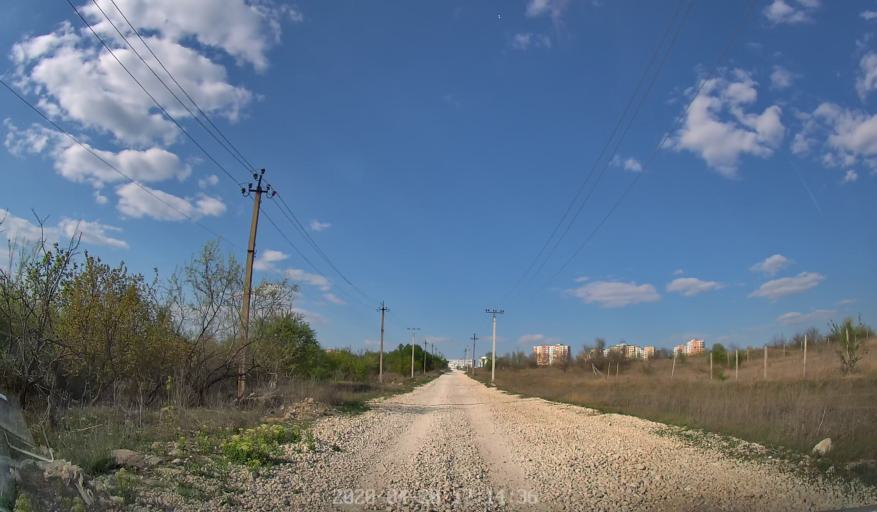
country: MD
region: Chisinau
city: Chisinau
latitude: 46.9682
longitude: 28.8437
